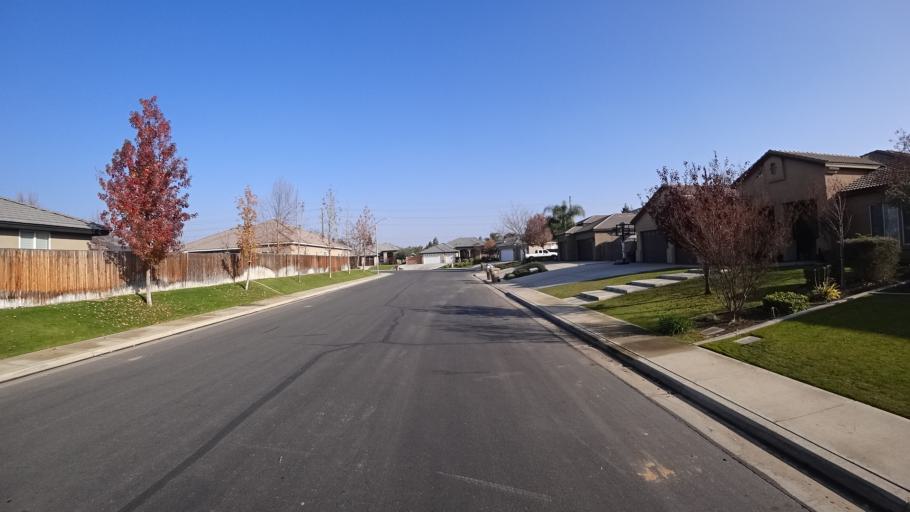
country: US
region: California
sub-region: Kern County
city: Greenacres
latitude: 35.4173
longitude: -119.0941
